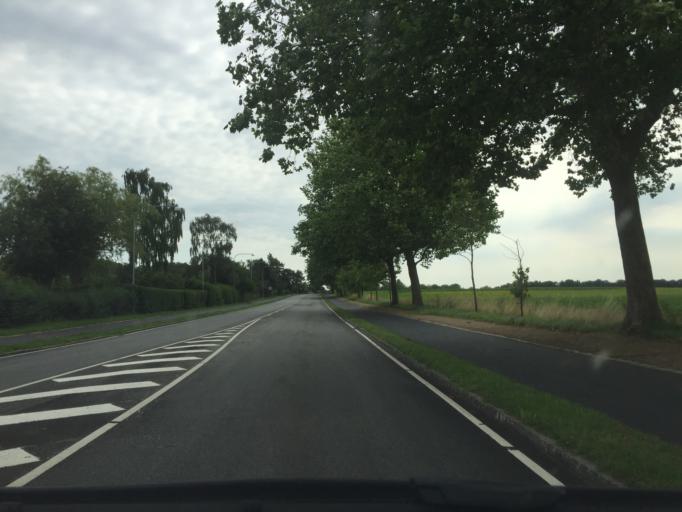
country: DK
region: Capital Region
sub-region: Lyngby-Tarbaek Kommune
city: Kongens Lyngby
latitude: 55.7863
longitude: 12.5417
